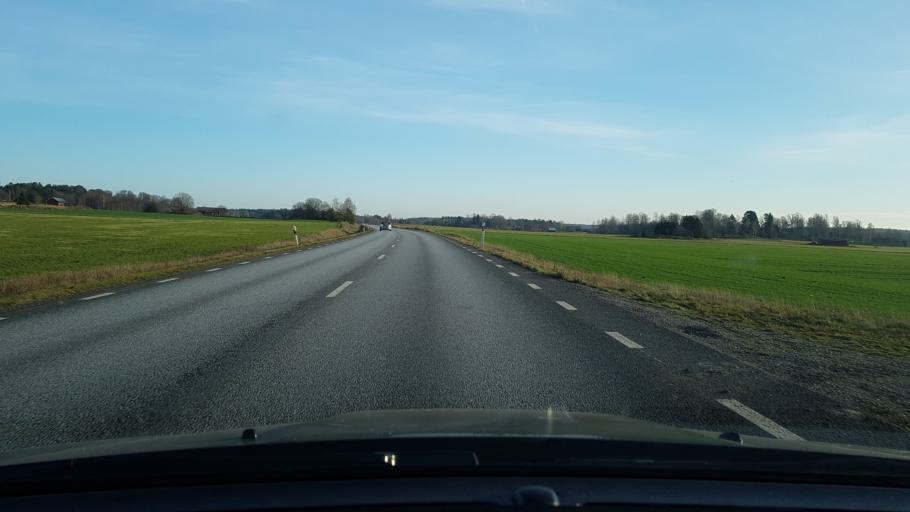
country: SE
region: Stockholm
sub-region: Vallentuna Kommun
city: Vallentuna
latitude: 59.7501
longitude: 18.0517
